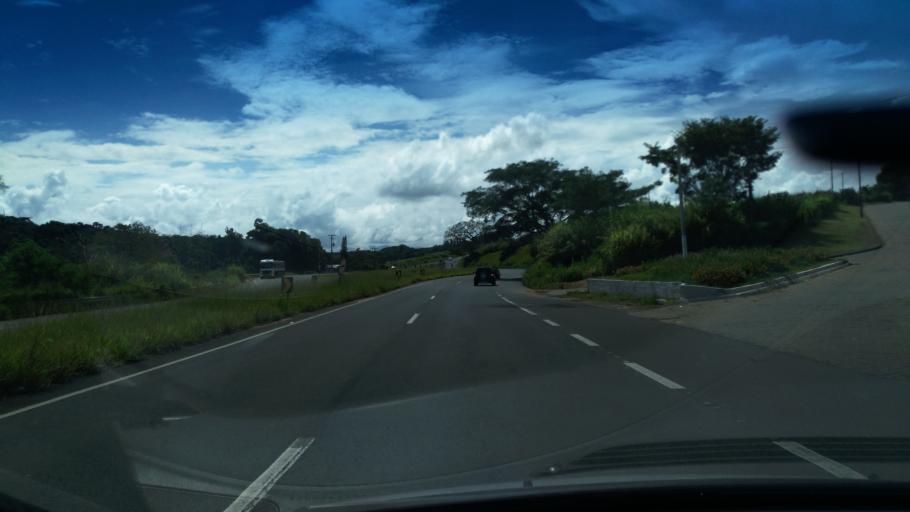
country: BR
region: Sao Paulo
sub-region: Santo Antonio Do Jardim
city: Espirito Santo do Pinhal
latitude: -22.1663
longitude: -46.7382
